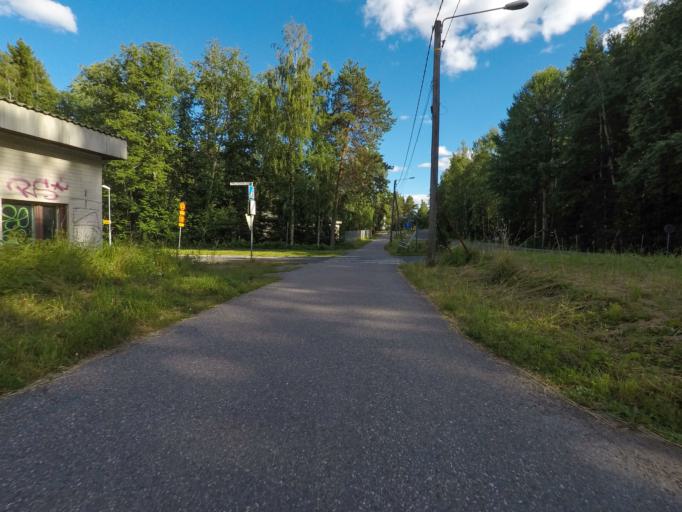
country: FI
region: South Karelia
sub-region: Lappeenranta
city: Lappeenranta
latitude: 61.0847
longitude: 28.1468
